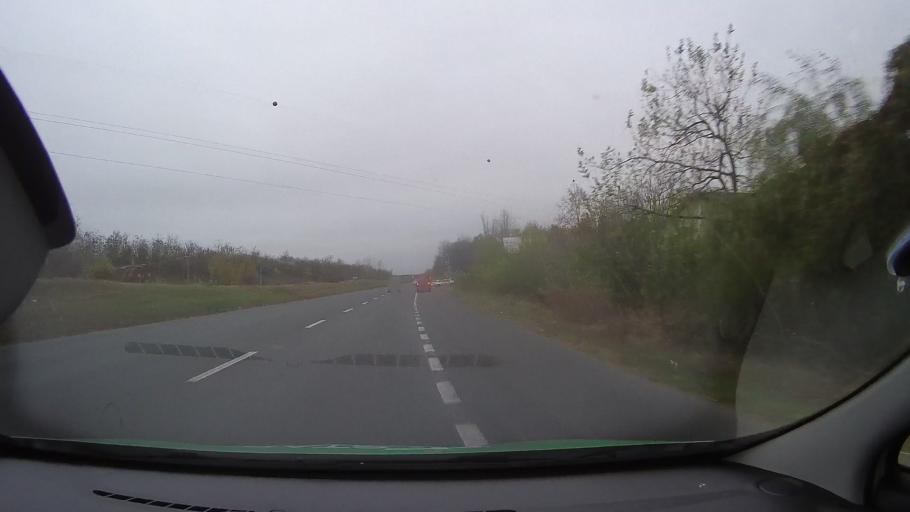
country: RO
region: Ialomita
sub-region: Comuna Slobozia
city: Slobozia
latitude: 44.5561
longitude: 27.3651
